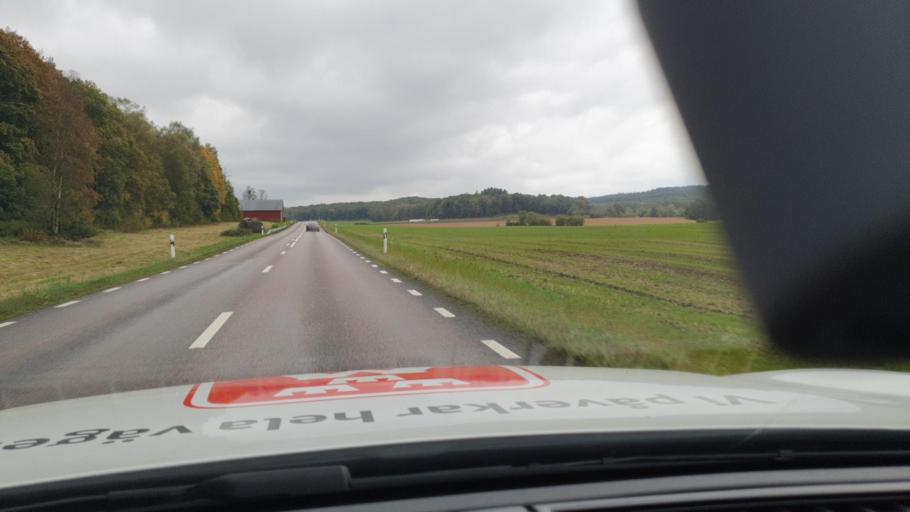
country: SE
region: Halland
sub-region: Falkenbergs Kommun
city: Falkenberg
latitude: 57.0473
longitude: 12.6086
